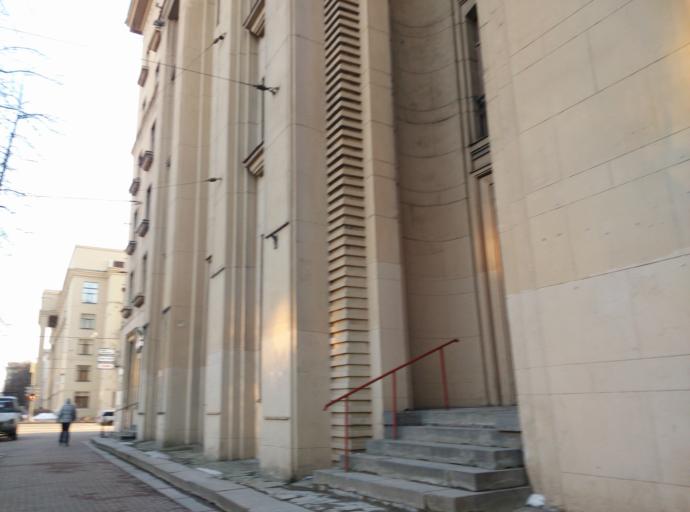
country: RU
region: St.-Petersburg
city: Kupchino
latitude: 59.8764
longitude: 30.3194
